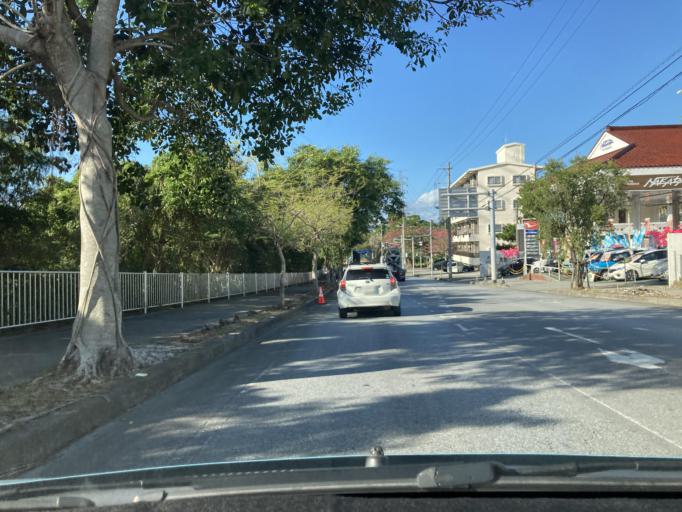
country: JP
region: Okinawa
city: Gushikawa
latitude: 26.3623
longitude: 127.8433
